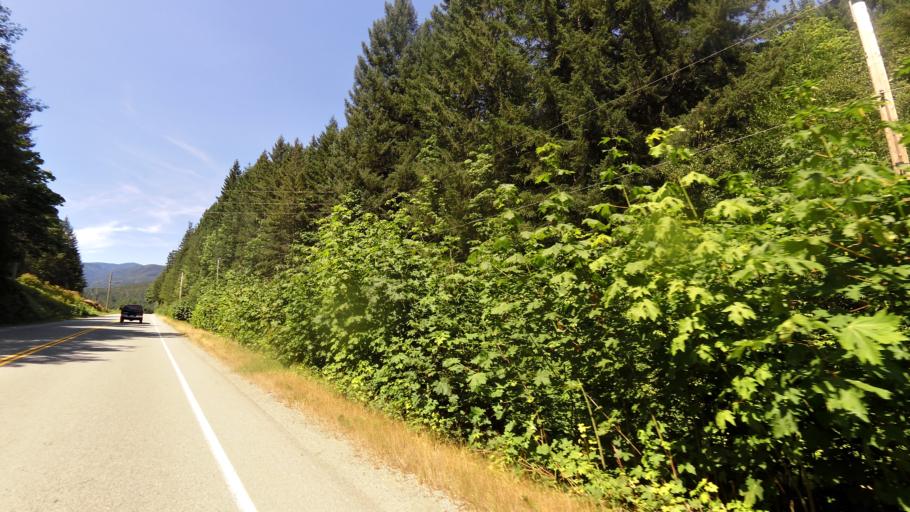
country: CA
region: British Columbia
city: Port Alberni
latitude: 49.2800
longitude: -124.9911
